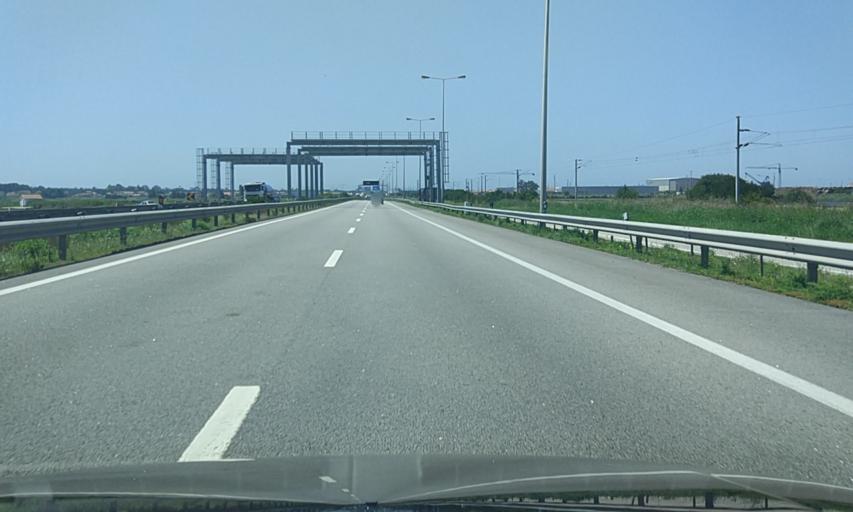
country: PT
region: Aveiro
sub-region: Aveiro
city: Aveiro
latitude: 40.6349
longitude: -8.6738
